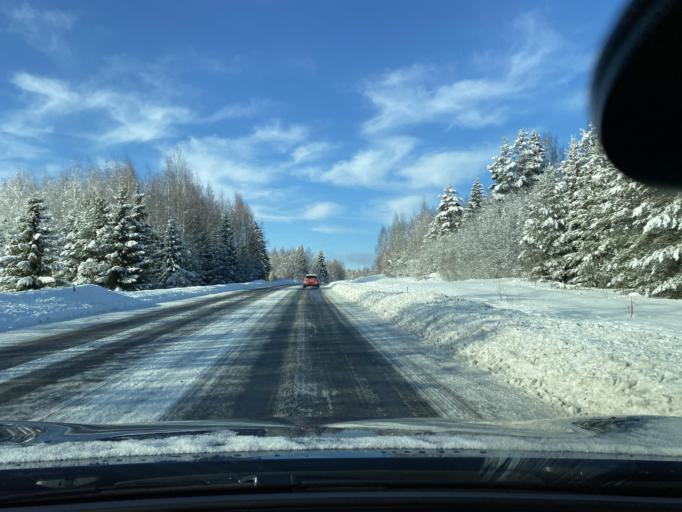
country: FI
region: Southern Savonia
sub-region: Mikkeli
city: Kangasniemi
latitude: 62.0127
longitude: 26.6271
